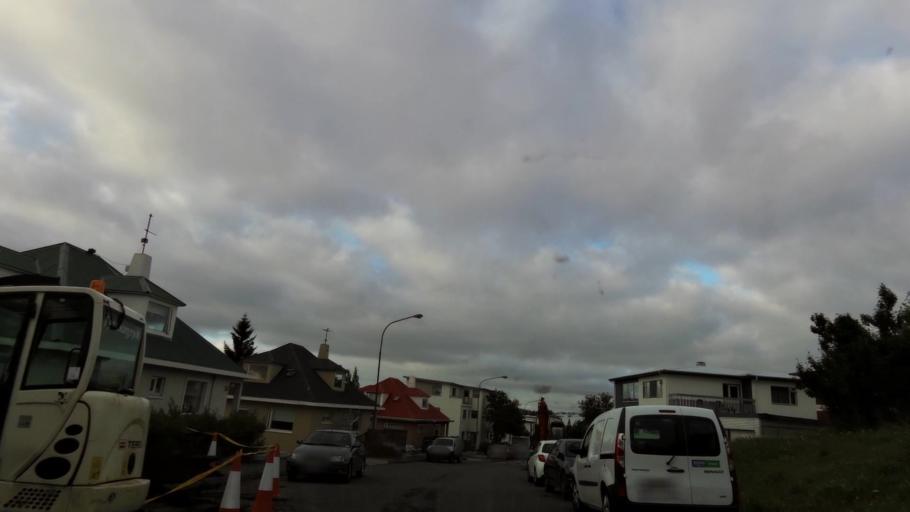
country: IS
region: Capital Region
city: Hafnarfjoerdur
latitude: 64.0623
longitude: -21.9512
